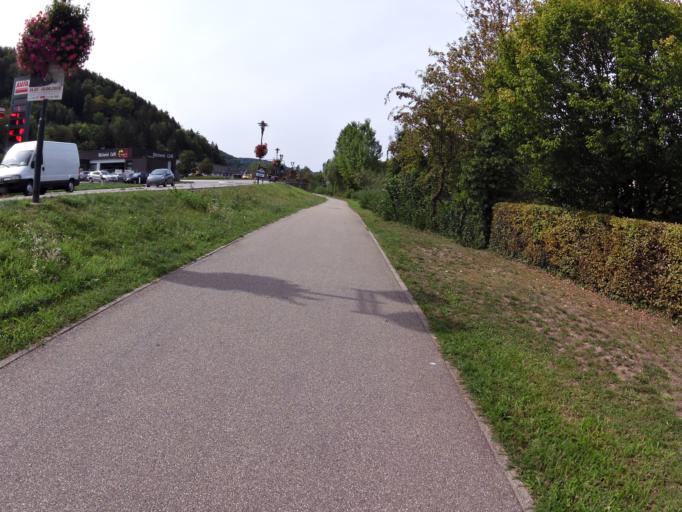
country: DE
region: Baden-Wuerttemberg
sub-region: Karlsruhe Region
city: Horb am Neckar
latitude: 48.4426
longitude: 8.6864
